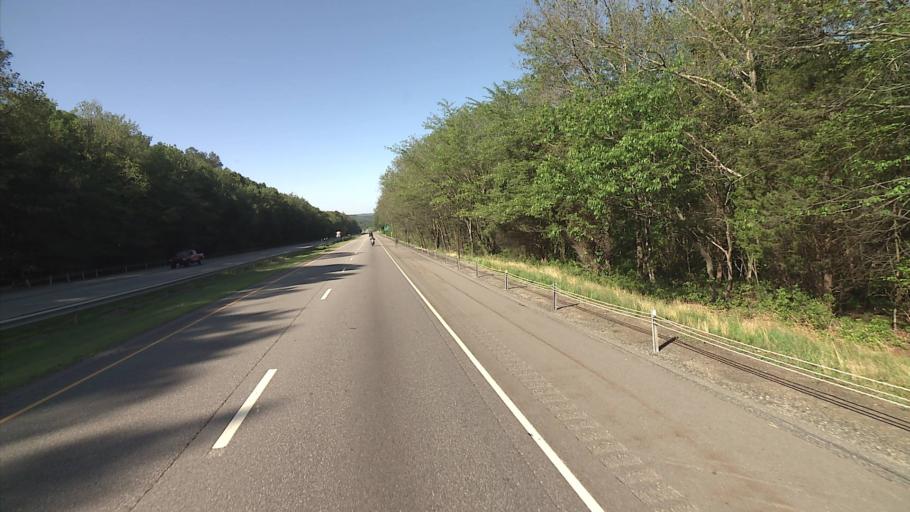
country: US
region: Connecticut
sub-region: New London County
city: Norwich
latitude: 41.5678
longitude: -72.0948
